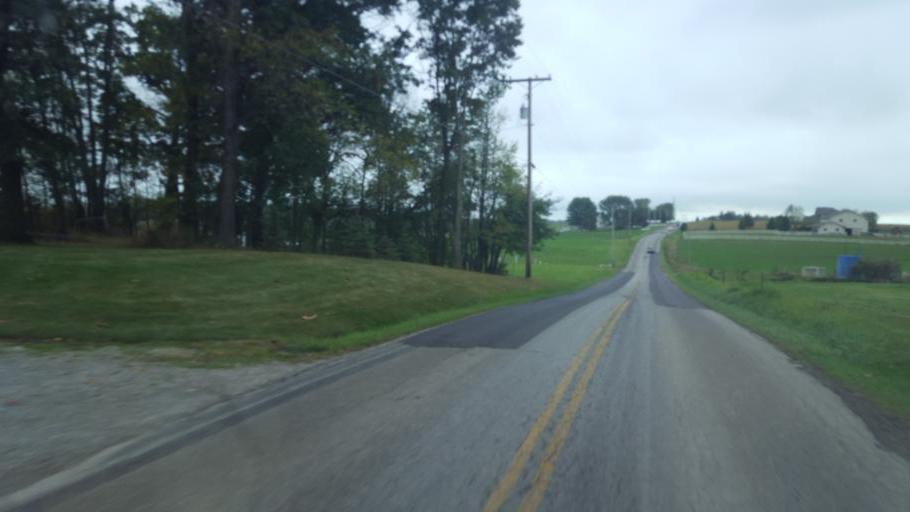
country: US
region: Ohio
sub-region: Wayne County
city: Apple Creek
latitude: 40.6406
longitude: -81.8124
